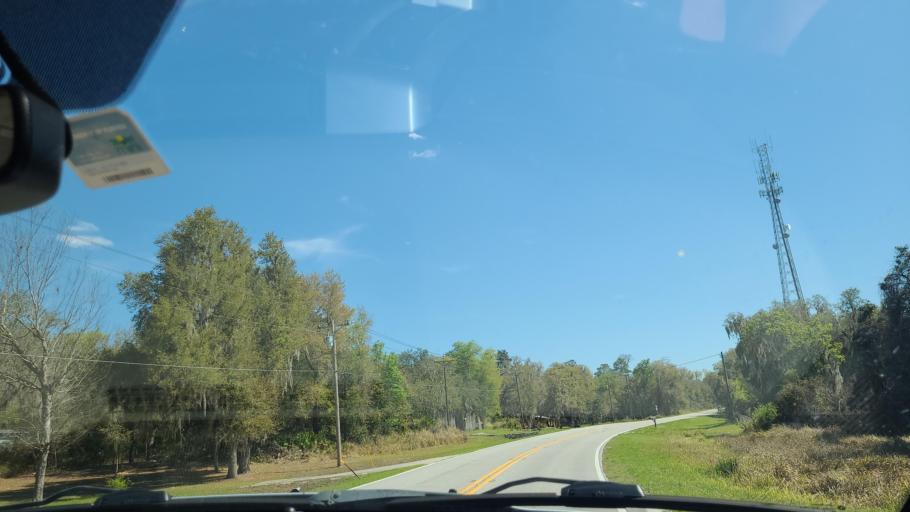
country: US
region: Florida
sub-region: Putnam County
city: Crescent City
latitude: 29.3726
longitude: -81.7436
